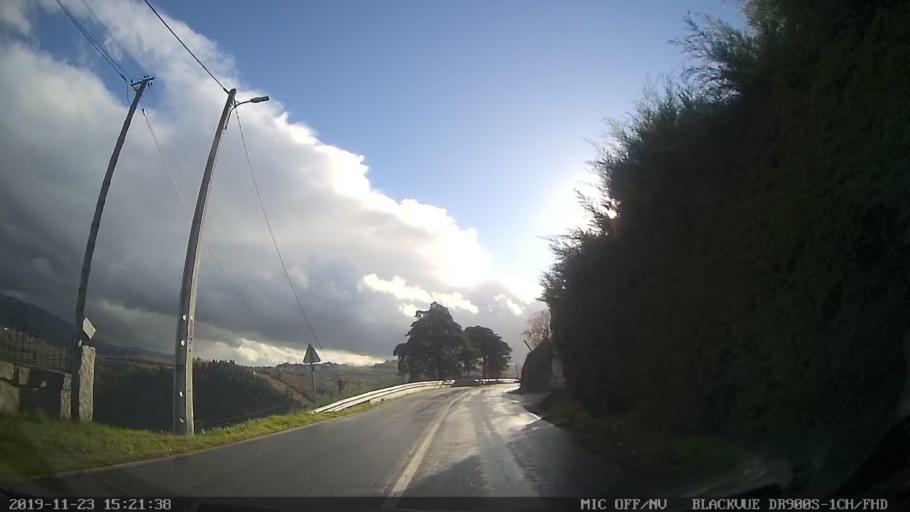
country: PT
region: Viseu
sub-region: Lamego
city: Lamego
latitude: 41.1100
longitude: -7.7898
